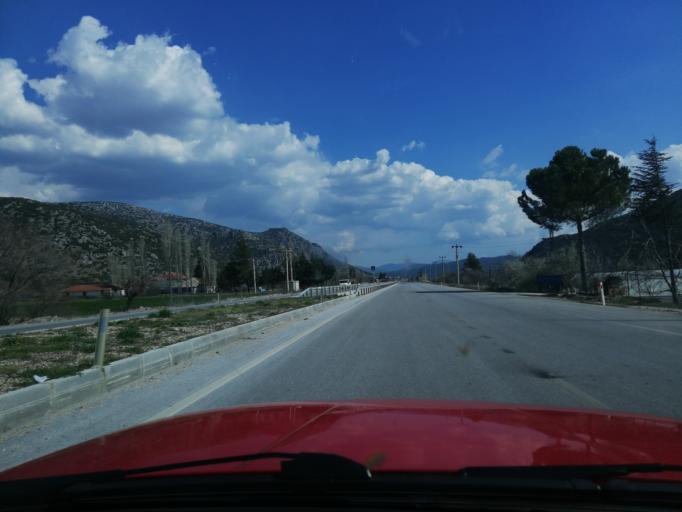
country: TR
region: Burdur
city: Celtikci
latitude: 37.5515
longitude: 30.4596
